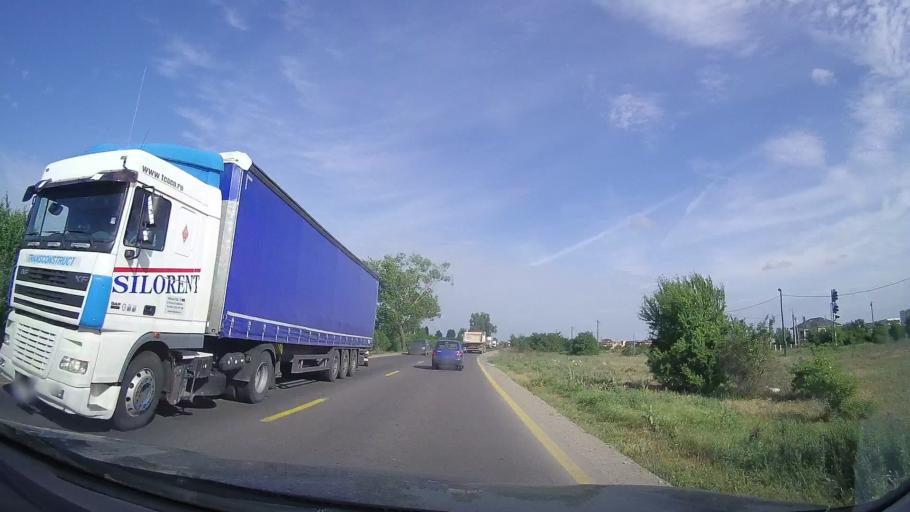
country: RO
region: Ilfov
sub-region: Comuna Magurele
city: Varteju
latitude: 44.3721
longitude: 26.0095
